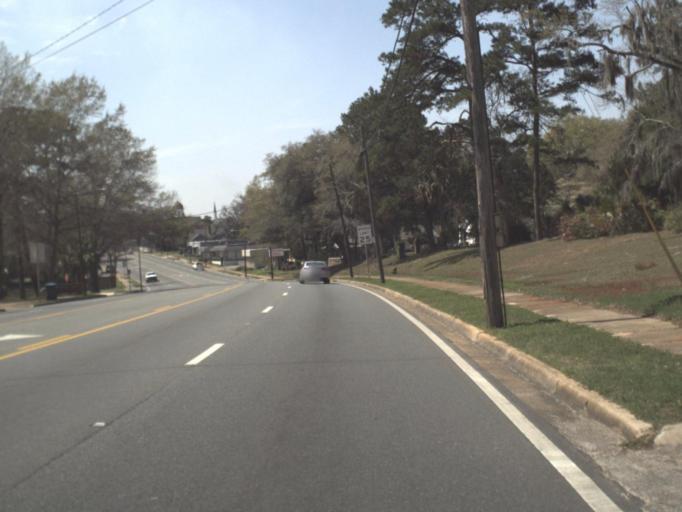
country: US
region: Florida
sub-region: Gadsden County
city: Quincy
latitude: 30.5879
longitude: -84.5701
